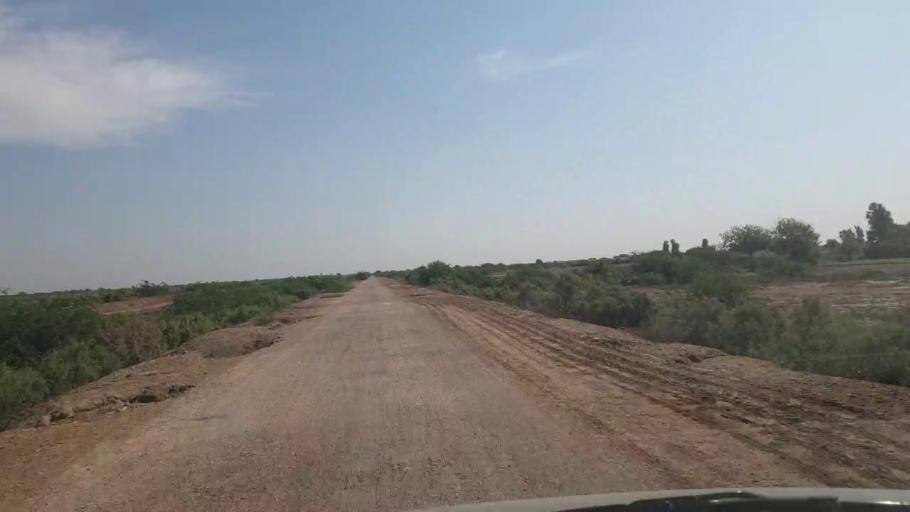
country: PK
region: Sindh
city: Digri
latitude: 24.9655
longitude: 69.1190
